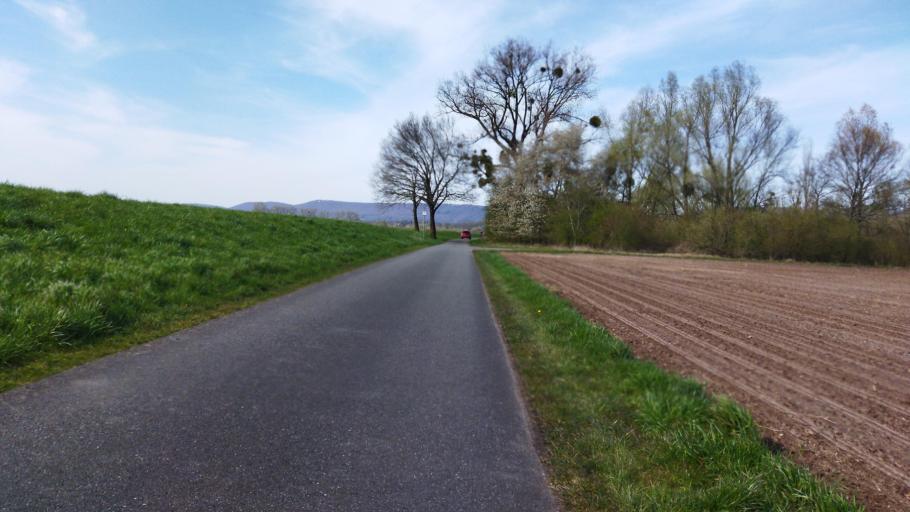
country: DE
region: Lower Saxony
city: Hessisch Oldendorf
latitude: 52.1543
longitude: 9.2722
